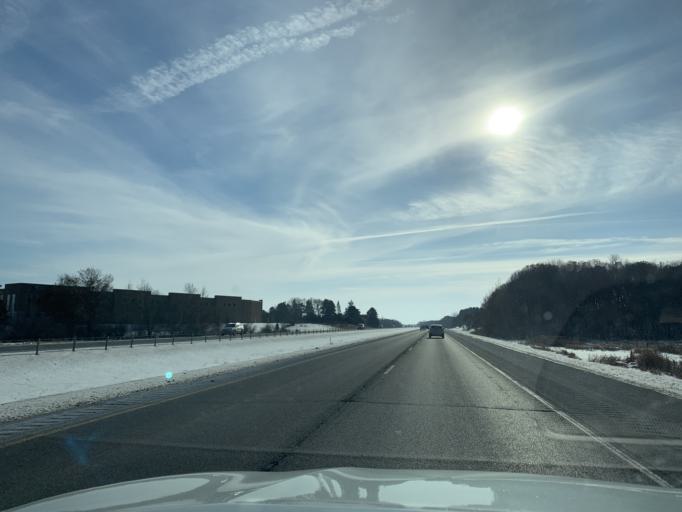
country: US
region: Minnesota
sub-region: Chisago County
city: Wyoming
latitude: 45.3190
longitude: -93.0036
